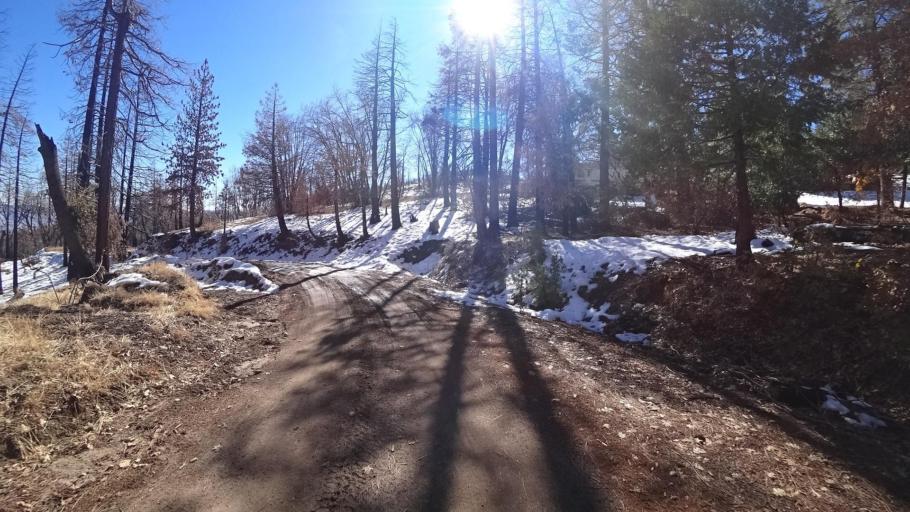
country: US
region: California
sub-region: Kern County
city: Alta Sierra
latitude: 35.7207
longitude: -118.5443
